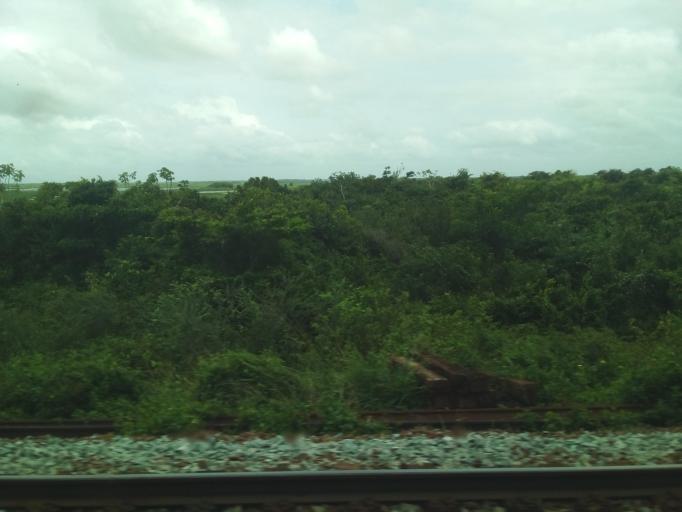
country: BR
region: Maranhao
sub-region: Arari
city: Arari
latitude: -3.5772
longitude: -44.7562
